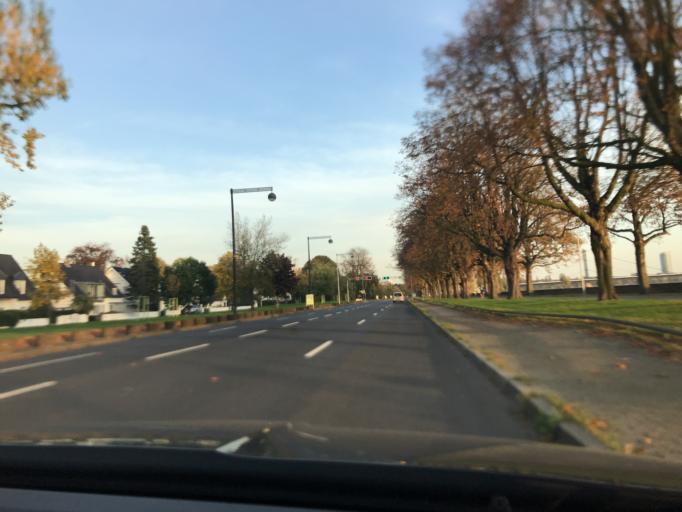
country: DE
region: North Rhine-Westphalia
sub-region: Regierungsbezirk Dusseldorf
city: Dusseldorf
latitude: 51.2525
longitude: 6.7512
